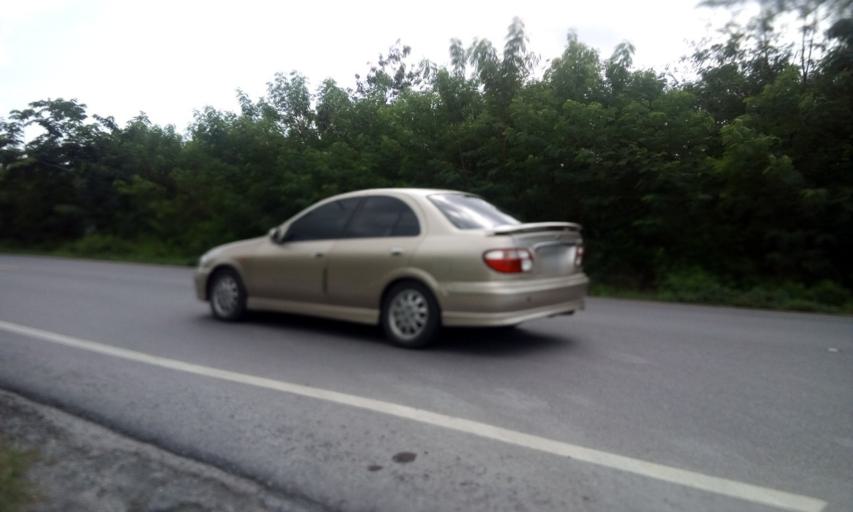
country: TH
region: Pathum Thani
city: Ban Lam Luk Ka
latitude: 13.9866
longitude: 100.8415
